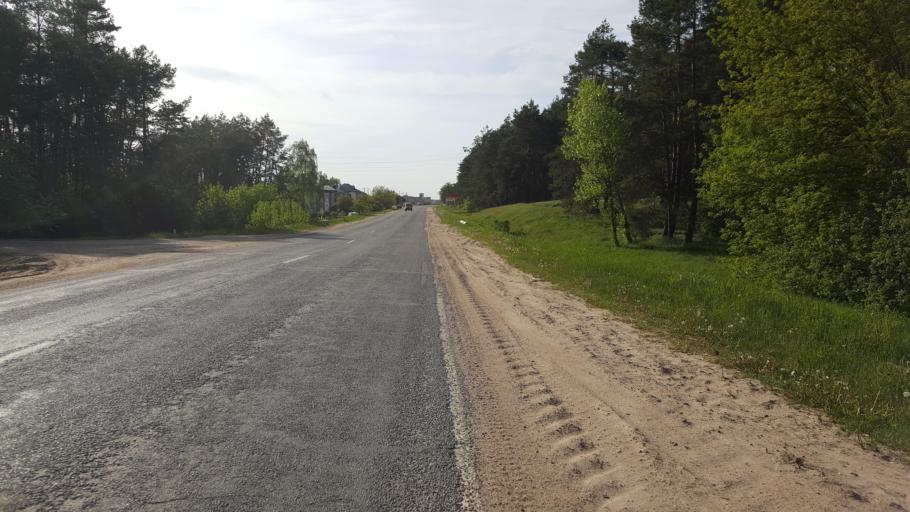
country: BY
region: Brest
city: Kamyanyets
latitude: 52.3914
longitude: 23.8382
